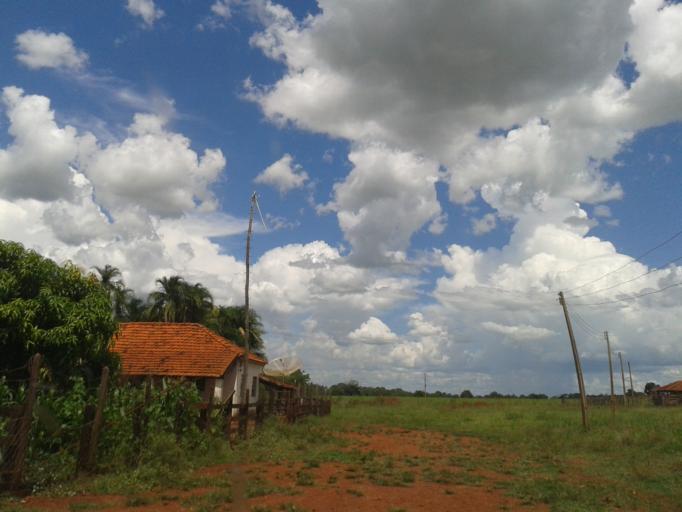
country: BR
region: Minas Gerais
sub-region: Capinopolis
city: Capinopolis
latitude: -18.7902
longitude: -49.7987
